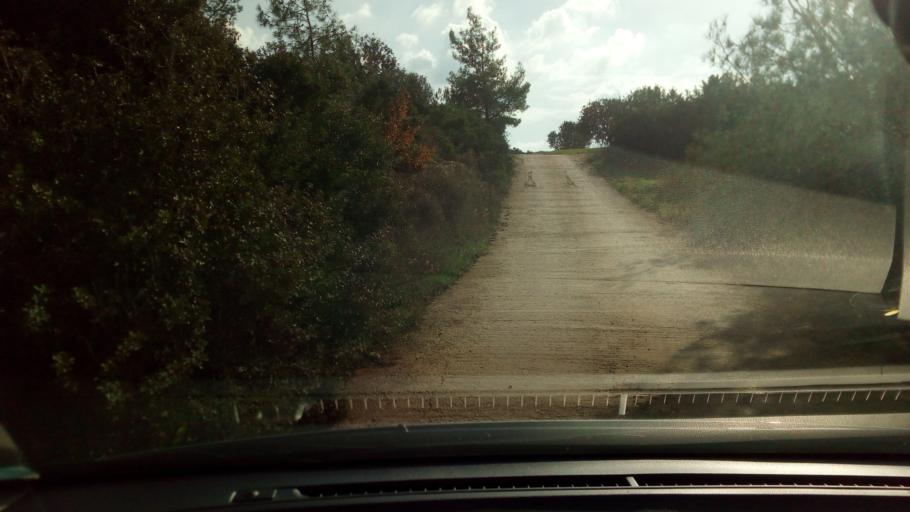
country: CY
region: Pafos
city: Polis
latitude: 35.0215
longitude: 32.3550
